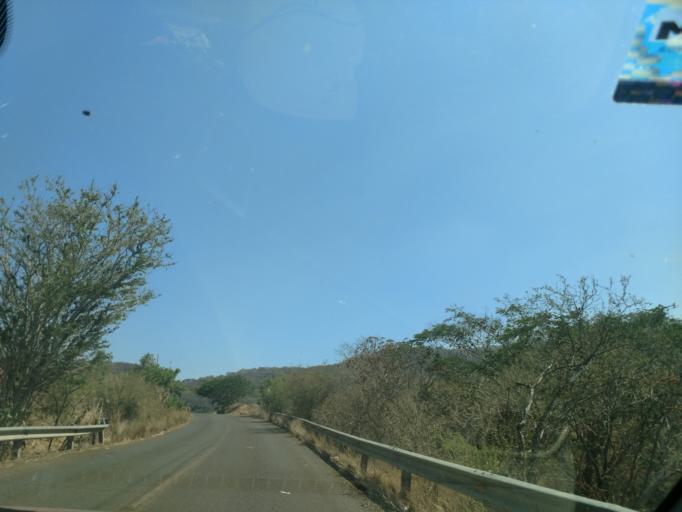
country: MX
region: Nayarit
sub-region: Tepic
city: La Corregidora
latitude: 21.4855
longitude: -104.6771
